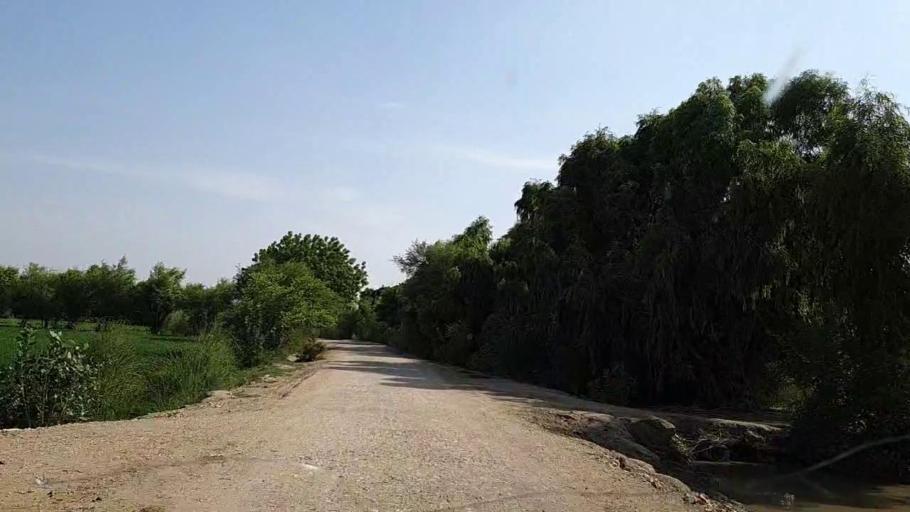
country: PK
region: Sindh
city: Khanpur
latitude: 27.7108
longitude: 69.3621
